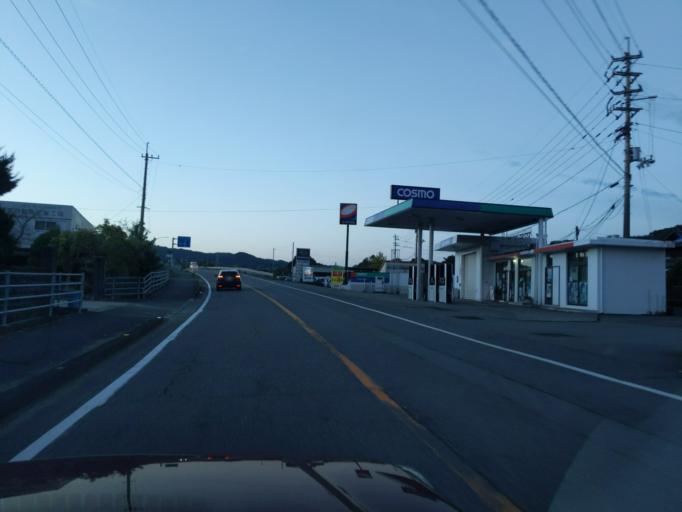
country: JP
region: Tokushima
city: Anan
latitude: 33.8506
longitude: 134.6261
